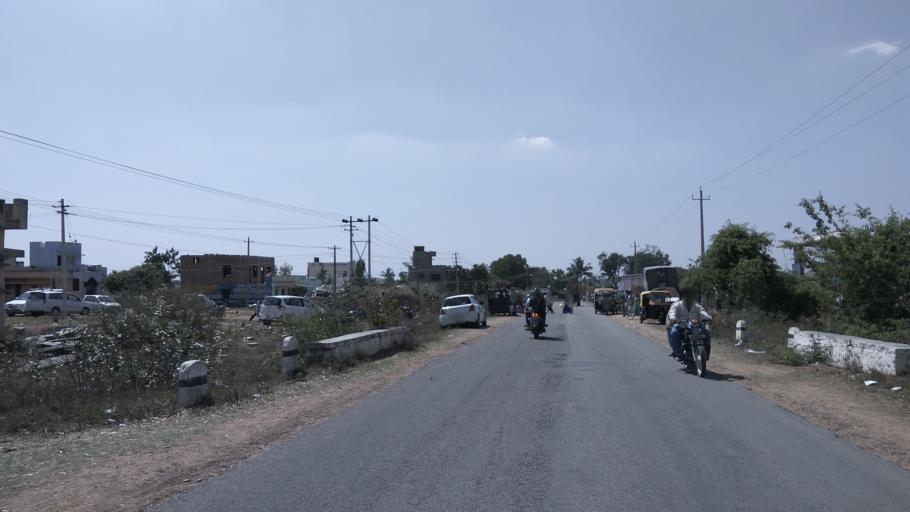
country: IN
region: Karnataka
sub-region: Kolar
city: Mulbagal
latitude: 13.1666
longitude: 78.3660
